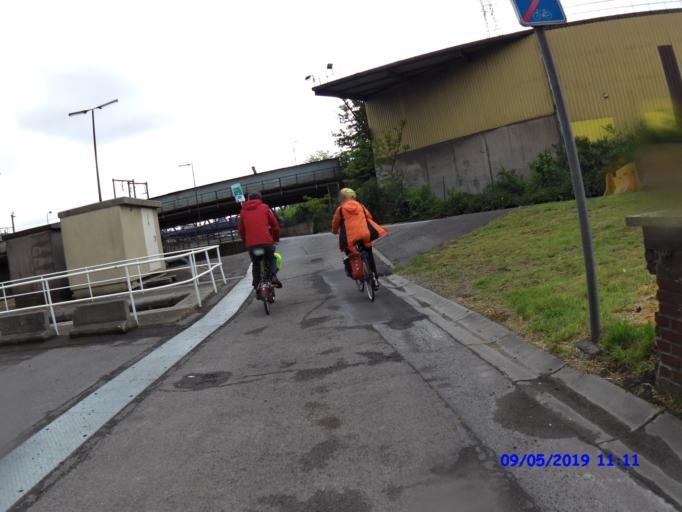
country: BE
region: Wallonia
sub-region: Province du Hainaut
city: Charleroi
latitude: 50.4078
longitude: 4.4303
